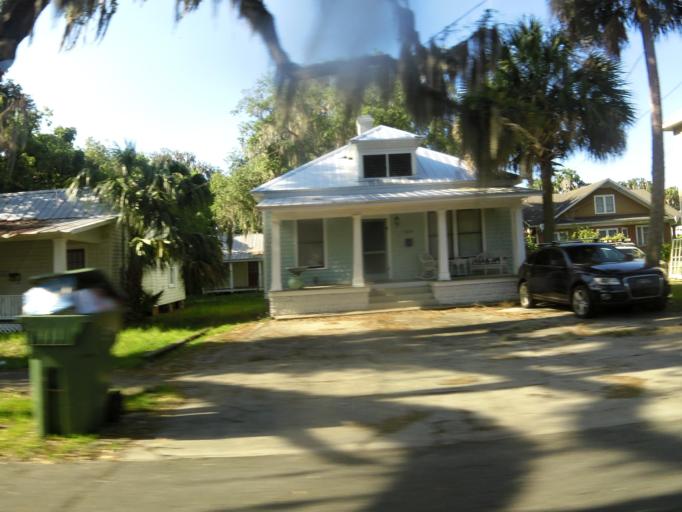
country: US
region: Florida
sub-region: Putnam County
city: Palatka
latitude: 29.6489
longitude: -81.6310
